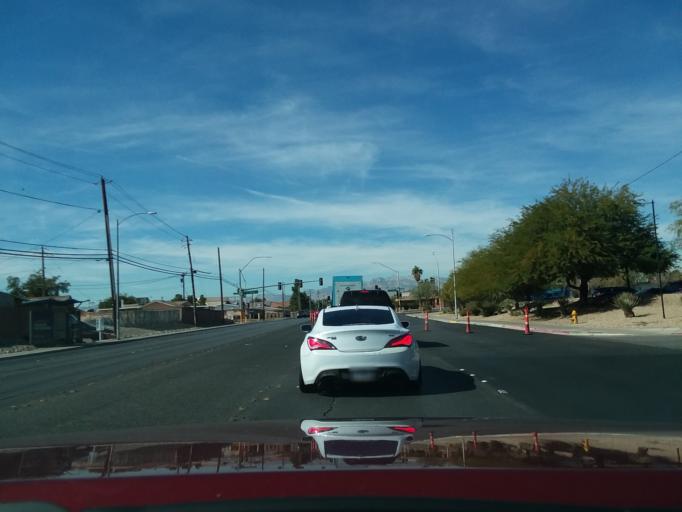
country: US
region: Nevada
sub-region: Clark County
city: Las Vegas
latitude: 36.1957
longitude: -115.1506
